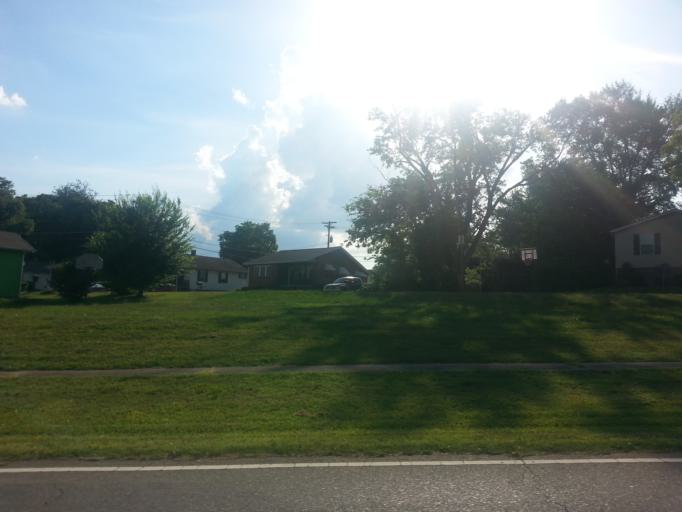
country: US
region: Tennessee
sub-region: Blount County
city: Alcoa
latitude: 35.7760
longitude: -83.9772
